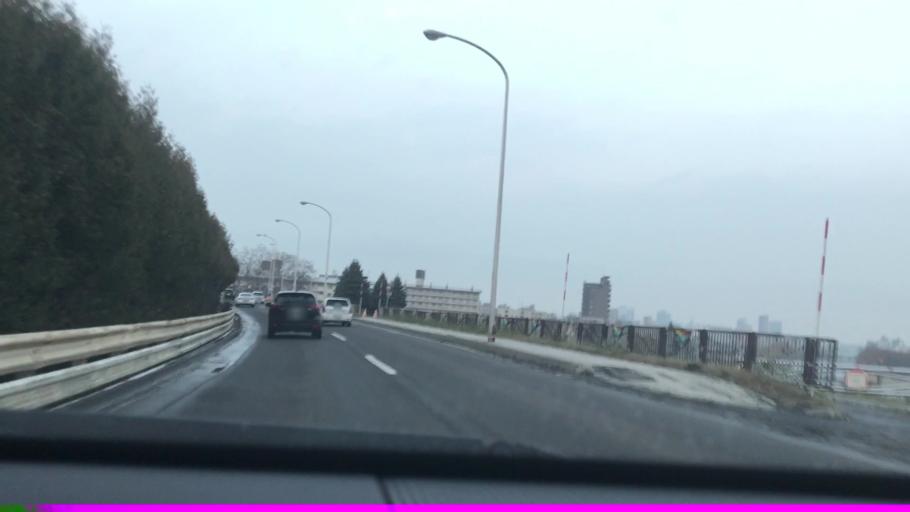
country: JP
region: Hokkaido
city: Sapporo
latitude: 43.0199
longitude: 141.3515
